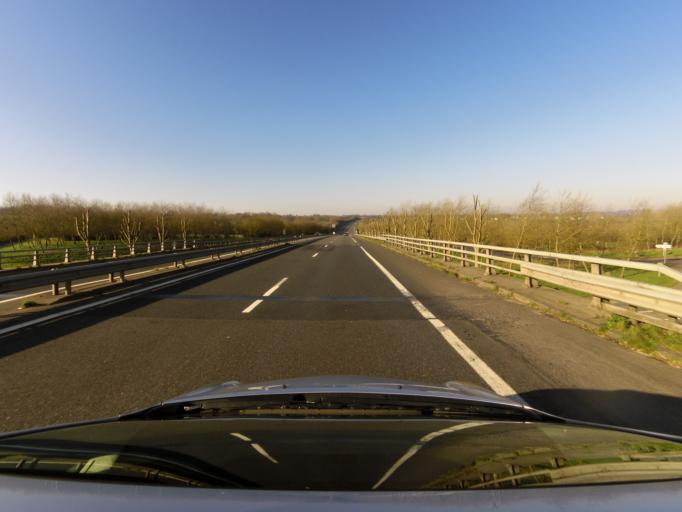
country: FR
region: Lower Normandy
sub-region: Departement du Calvados
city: Saint-Martin-des-Besaces
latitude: 49.0253
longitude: -0.8333
